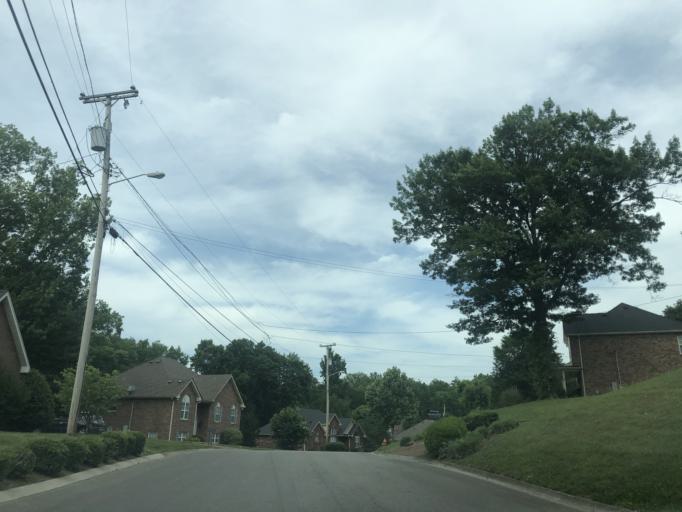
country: US
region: Tennessee
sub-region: Davidson County
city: Nashville
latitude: 36.2110
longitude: -86.8103
